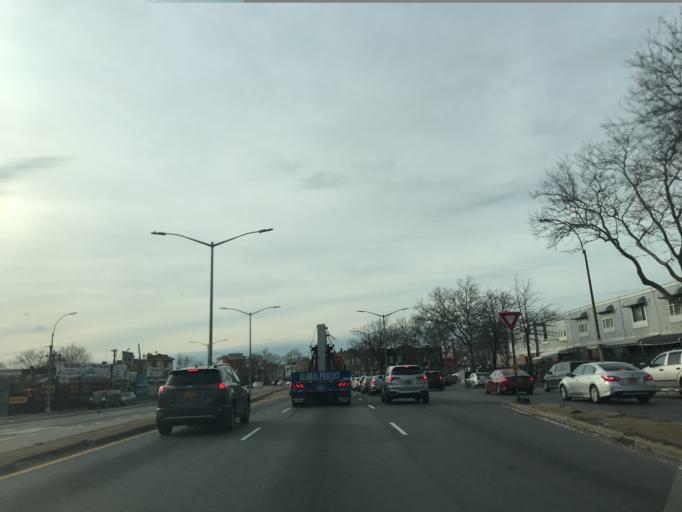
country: US
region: New York
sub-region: Kings County
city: East New York
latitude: 40.6577
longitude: -73.8944
